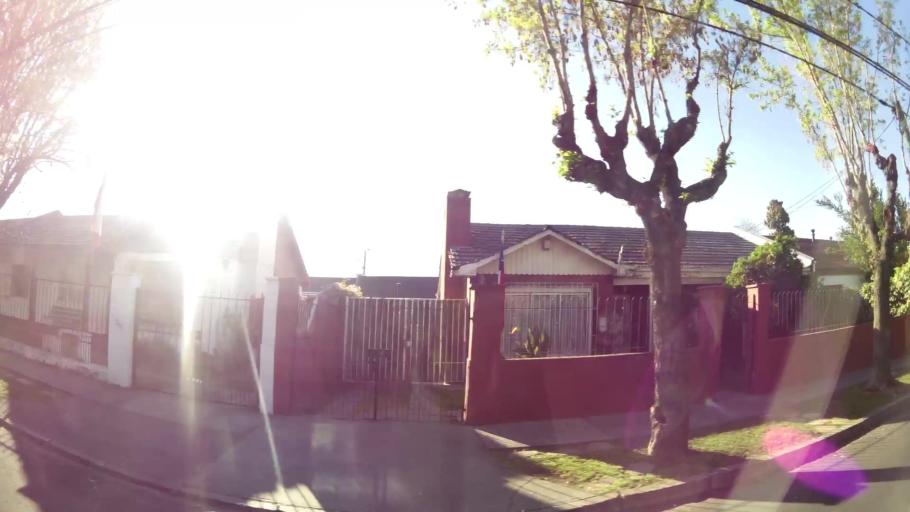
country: CL
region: Santiago Metropolitan
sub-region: Provincia de Santiago
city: Villa Presidente Frei, Nunoa, Santiago, Chile
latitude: -33.4602
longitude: -70.5650
